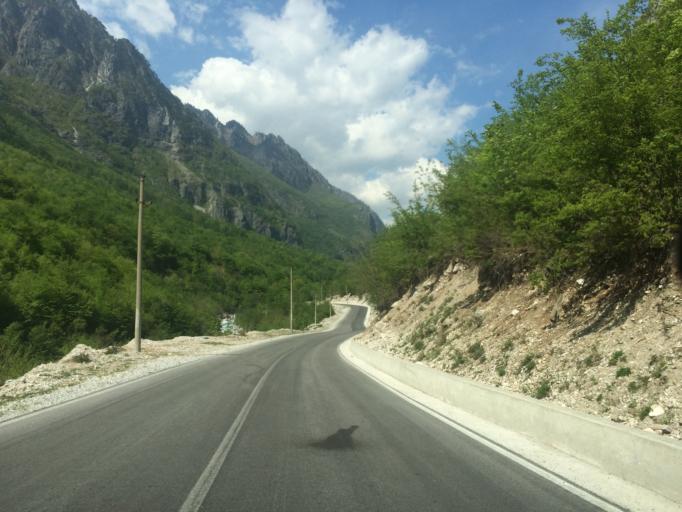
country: AL
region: Kukes
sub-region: Rrethi i Tropojes
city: Bajram Curri
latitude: 42.3956
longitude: 20.0527
